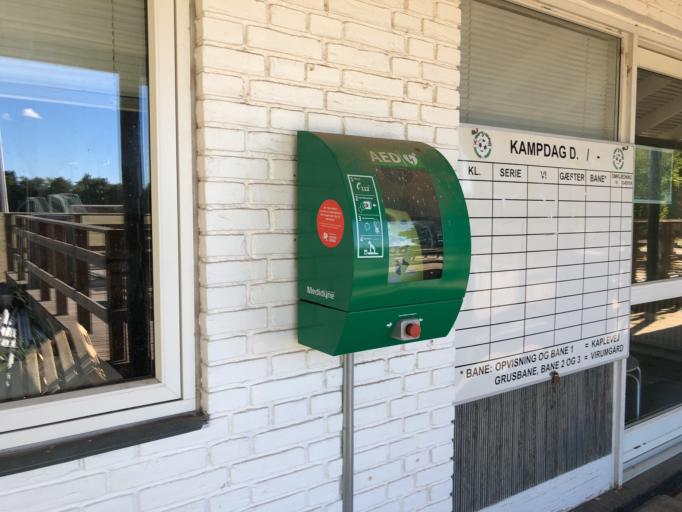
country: DK
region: Capital Region
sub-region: Rudersdal Kommune
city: Holte
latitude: 55.7862
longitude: 12.4709
